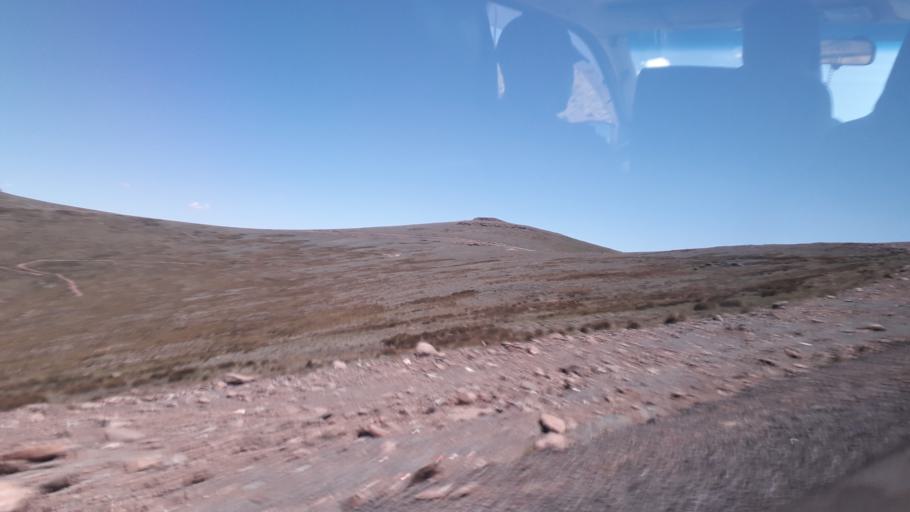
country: ZA
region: Orange Free State
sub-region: Thabo Mofutsanyana District Municipality
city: Phuthaditjhaba
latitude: -28.8176
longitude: 28.7356
